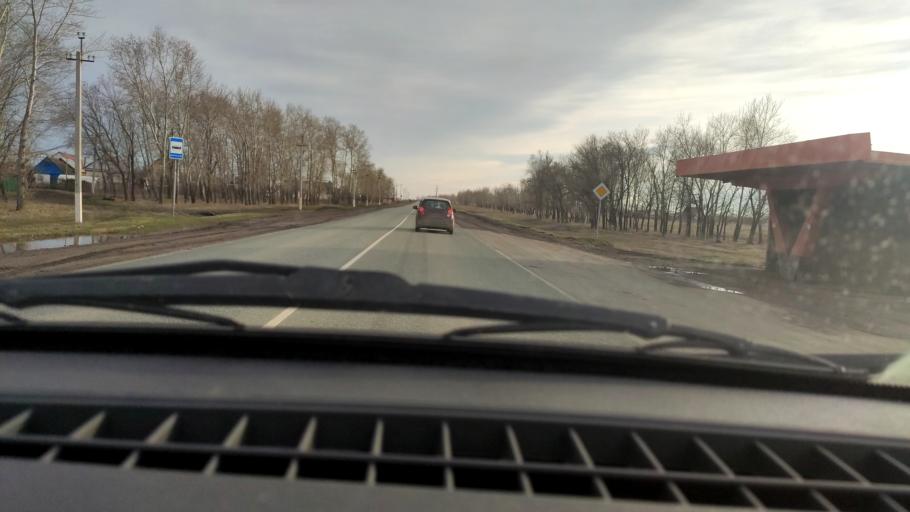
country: RU
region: Bashkortostan
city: Davlekanovo
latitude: 54.3908
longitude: 55.2029
